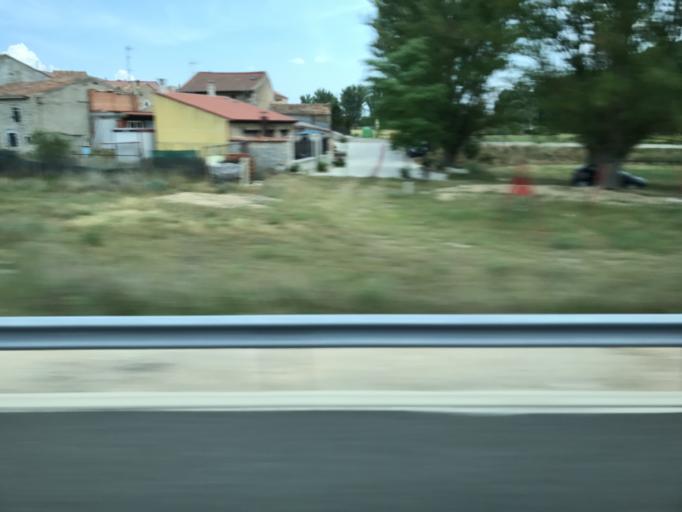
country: ES
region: Castille and Leon
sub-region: Provincia de Burgos
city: Oquillas
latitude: 41.8298
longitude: -3.7079
